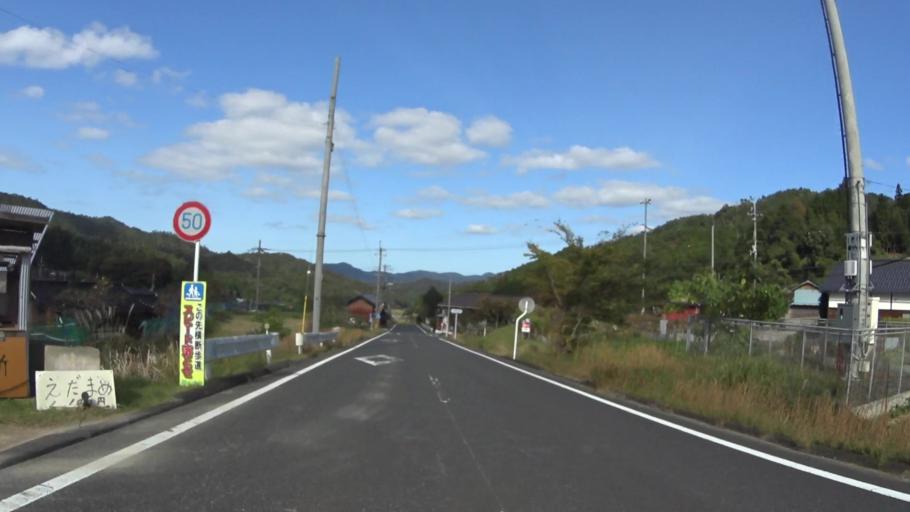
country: JP
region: Hyogo
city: Toyooka
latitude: 35.5450
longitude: 134.9781
